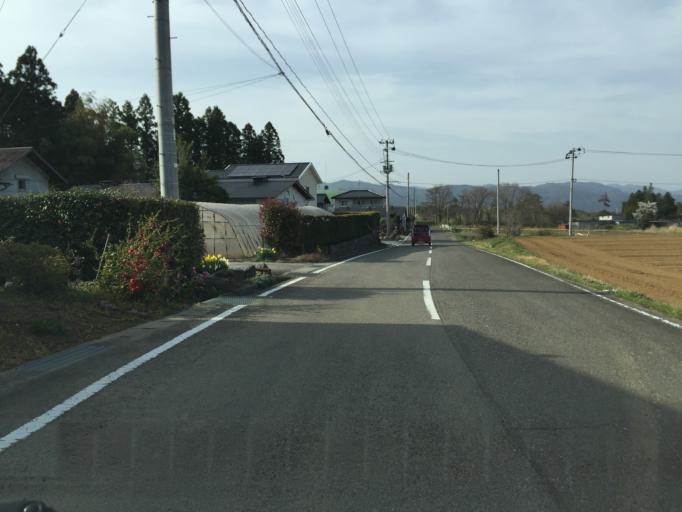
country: JP
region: Fukushima
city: Fukushima-shi
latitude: 37.7211
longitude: 140.3711
